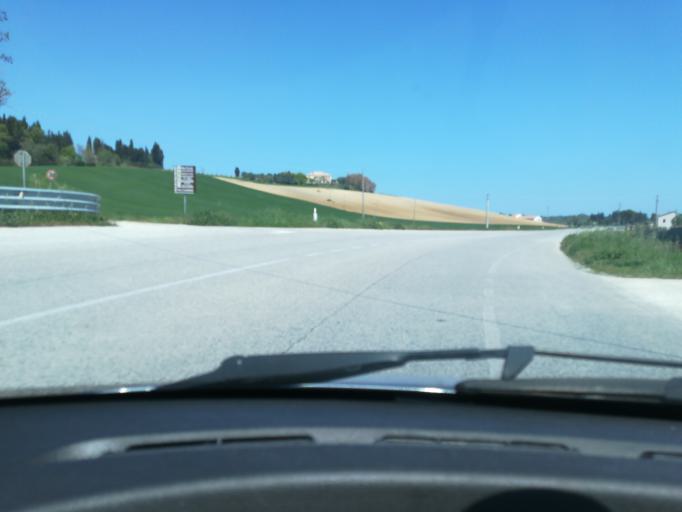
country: IT
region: The Marches
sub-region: Provincia di Ancona
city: Villa Musone
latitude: 43.4619
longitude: 13.5984
